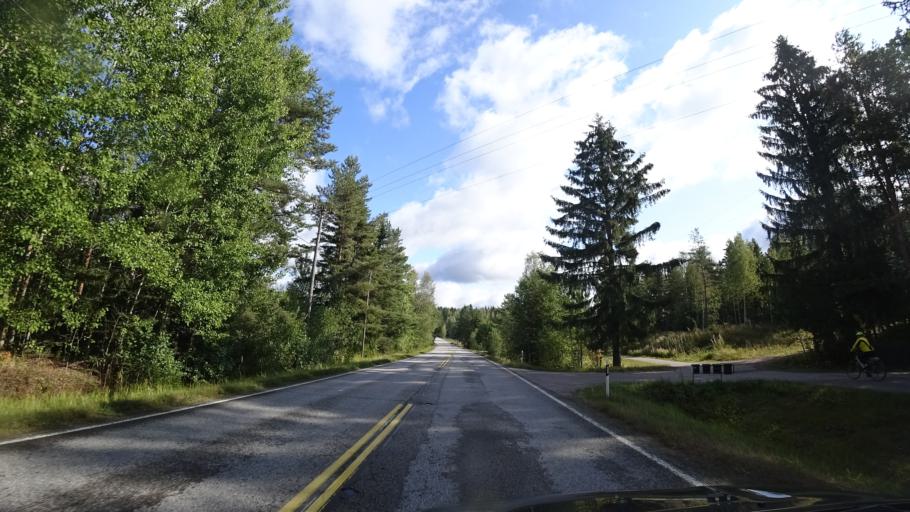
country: FI
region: Uusimaa
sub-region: Helsinki
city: Jaervenpaeae
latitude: 60.5812
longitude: 25.0001
